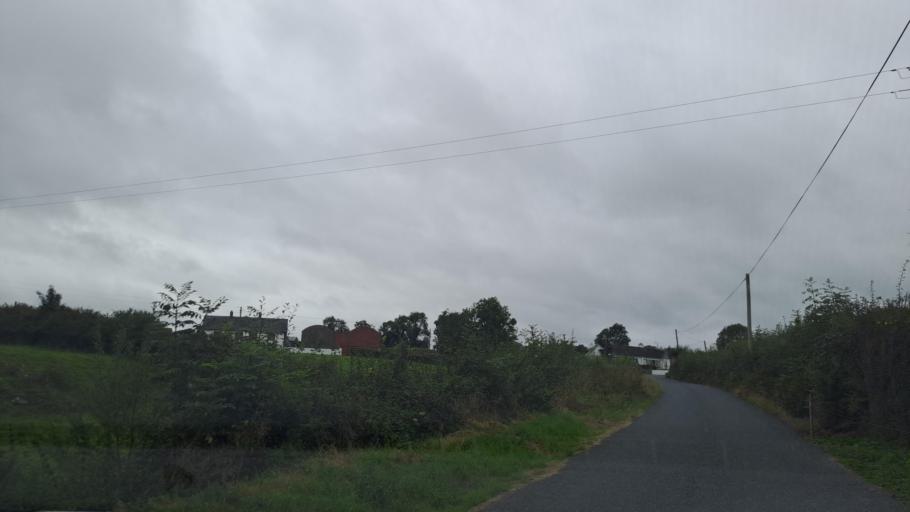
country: IE
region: Ulster
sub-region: An Cabhan
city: Kingscourt
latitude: 54.0084
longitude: -6.8713
